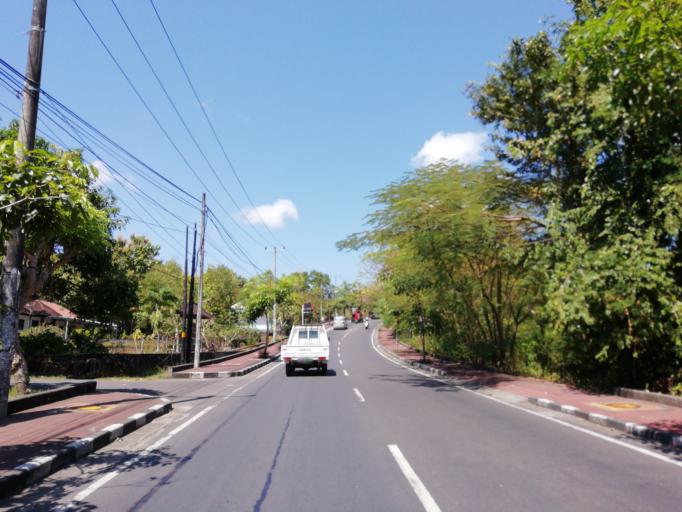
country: ID
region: Bali
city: Jimbaran
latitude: -8.7913
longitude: 115.1775
